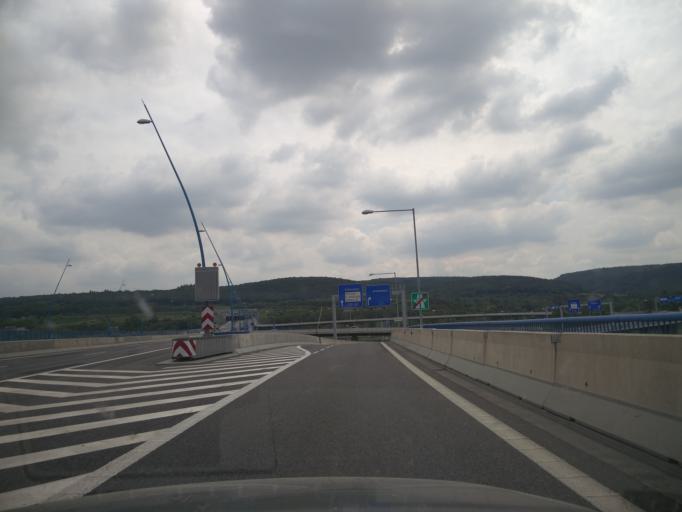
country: CZ
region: Praha
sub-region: Praha 12
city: Modrany
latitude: 49.9870
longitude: 14.3915
